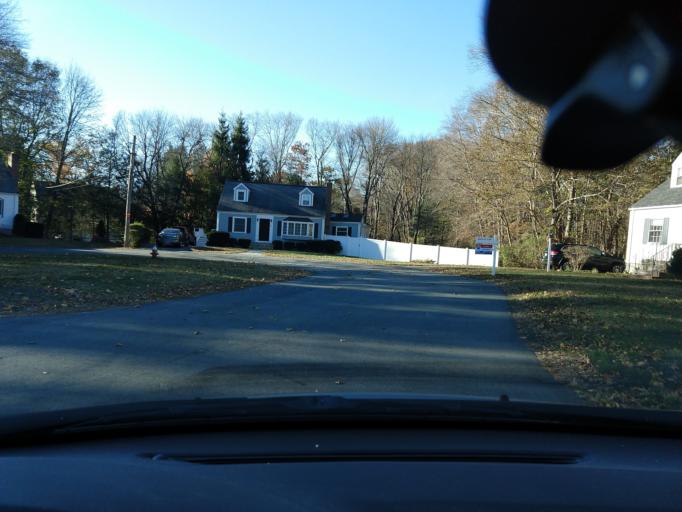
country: US
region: Massachusetts
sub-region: Middlesex County
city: Bedford
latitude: 42.4890
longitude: -71.2805
